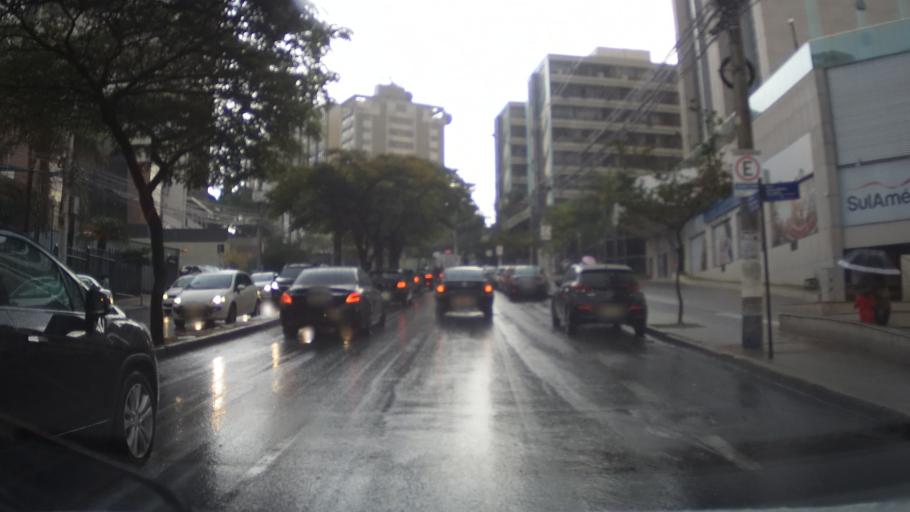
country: BR
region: Minas Gerais
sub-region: Belo Horizonte
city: Belo Horizonte
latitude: -19.9473
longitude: -43.9601
